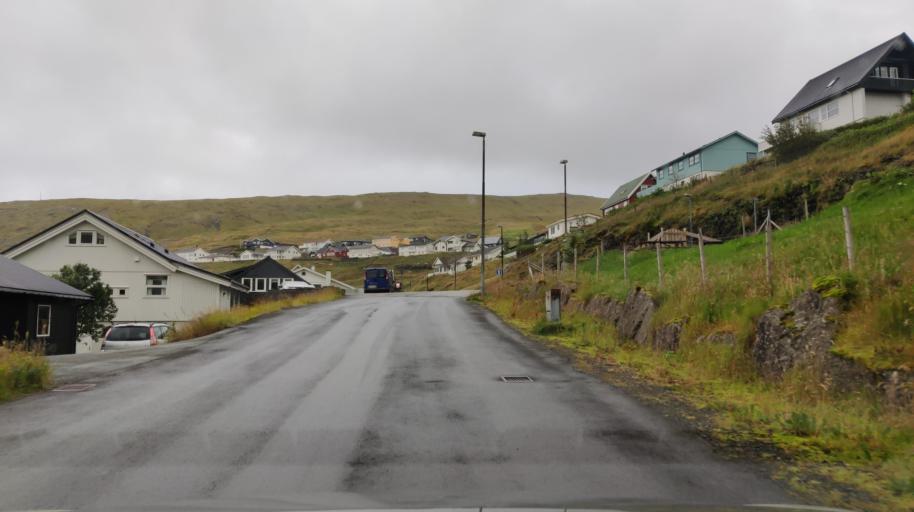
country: FO
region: Streymoy
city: Vestmanna
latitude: 62.1566
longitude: -7.1780
